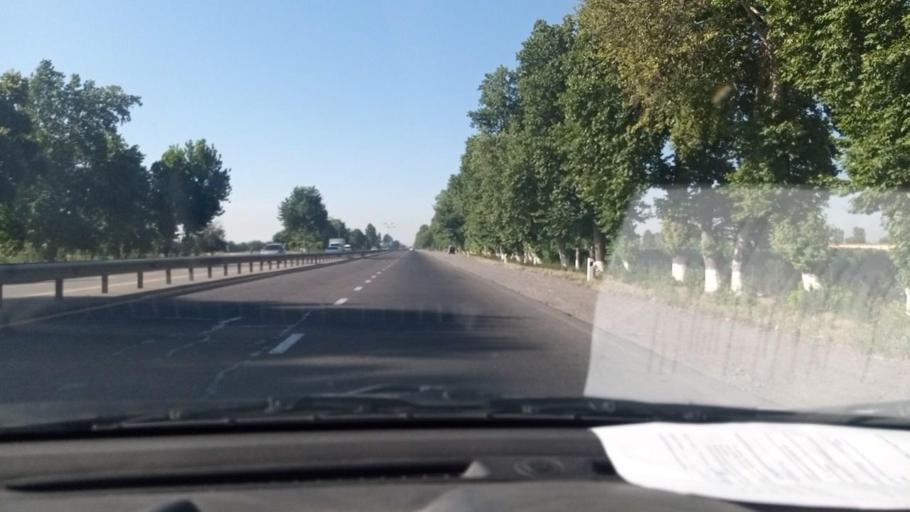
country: UZ
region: Toshkent Shahri
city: Bektemir
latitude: 41.2220
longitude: 69.4024
